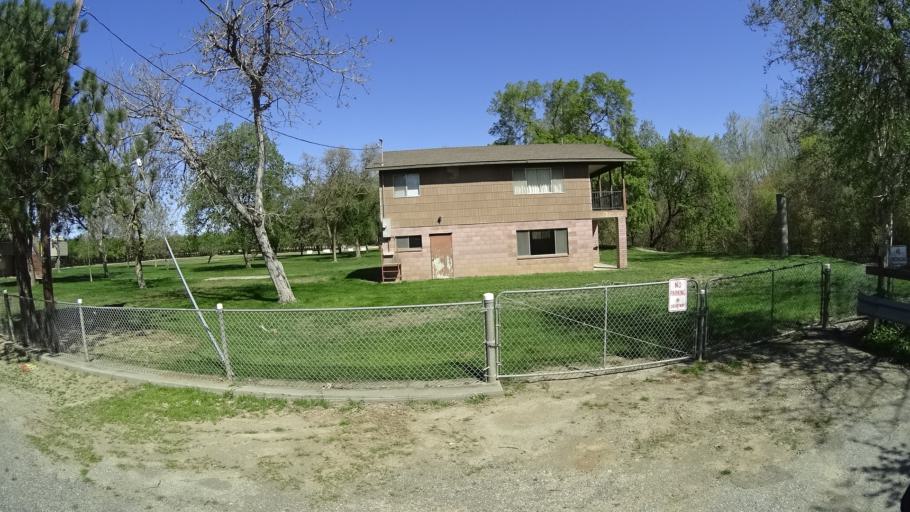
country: US
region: California
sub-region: Glenn County
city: Hamilton City
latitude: 39.7755
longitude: -122.0313
